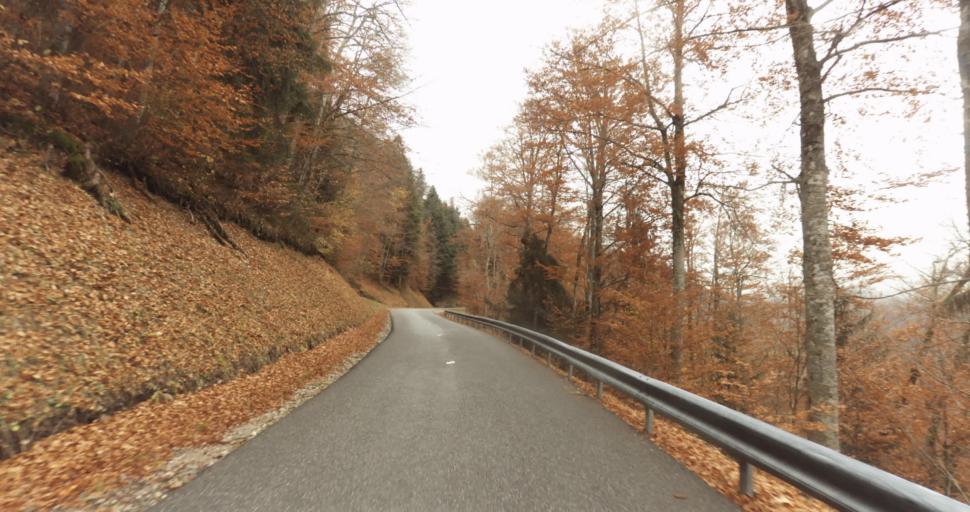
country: FR
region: Rhone-Alpes
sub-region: Departement de la Haute-Savoie
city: Thorens-Glieres
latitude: 45.9729
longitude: 6.2928
